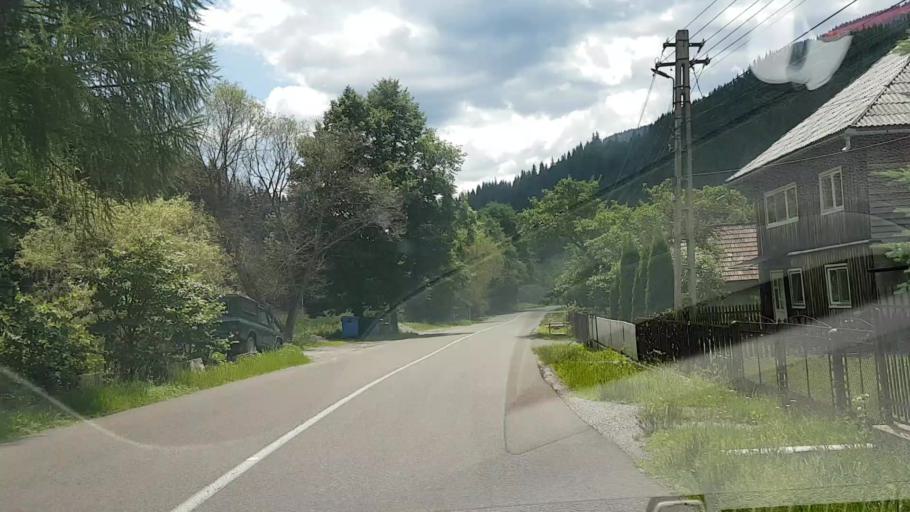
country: RO
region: Suceava
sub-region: Comuna Crucea
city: Crucea
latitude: 47.3423
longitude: 25.6109
